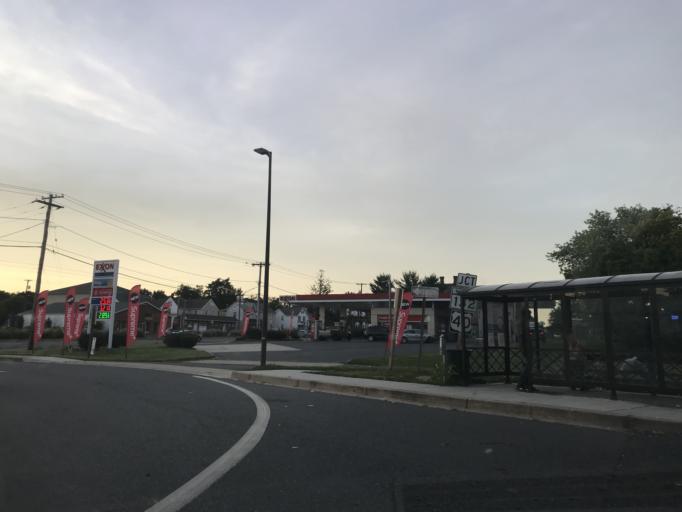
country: US
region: Maryland
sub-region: Harford County
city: Aberdeen
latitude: 39.5091
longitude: -76.1630
